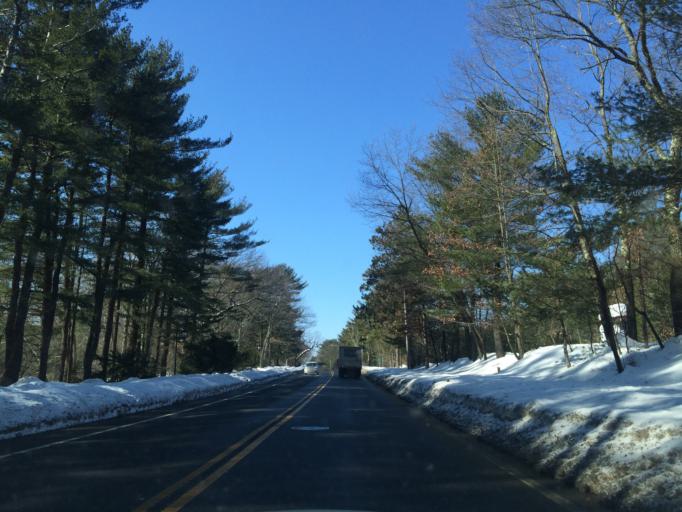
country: US
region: Massachusetts
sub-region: Norfolk County
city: Wellesley
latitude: 42.2962
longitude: -71.3034
